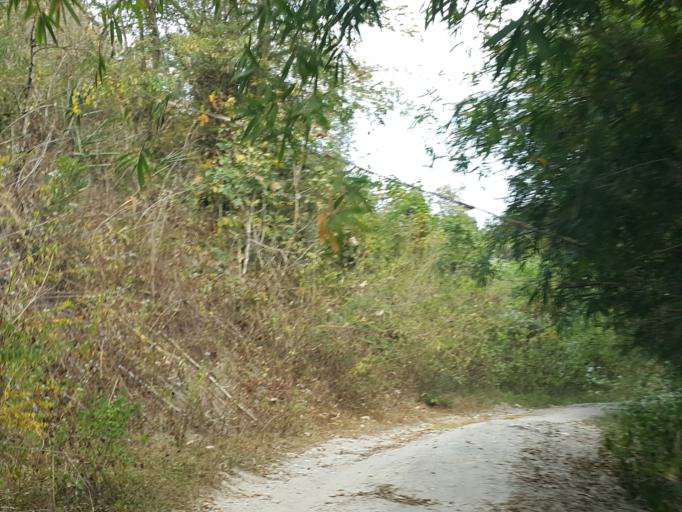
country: TH
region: Chiang Mai
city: Om Koi
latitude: 17.7964
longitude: 98.3404
